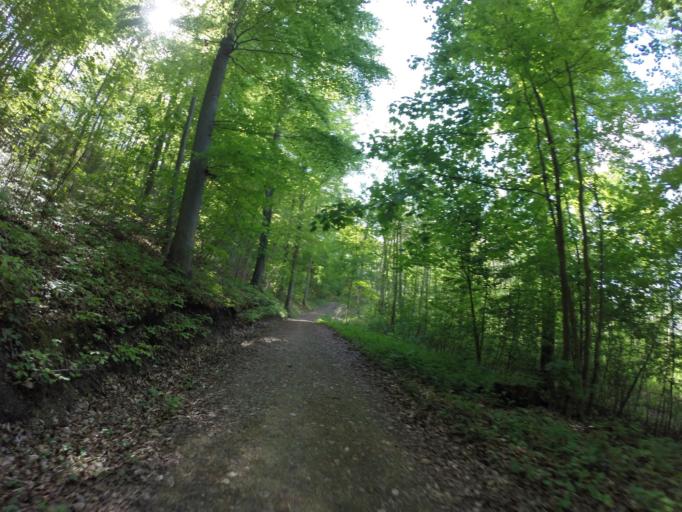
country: DE
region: Thuringia
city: Jena
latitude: 50.9248
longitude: 11.6196
